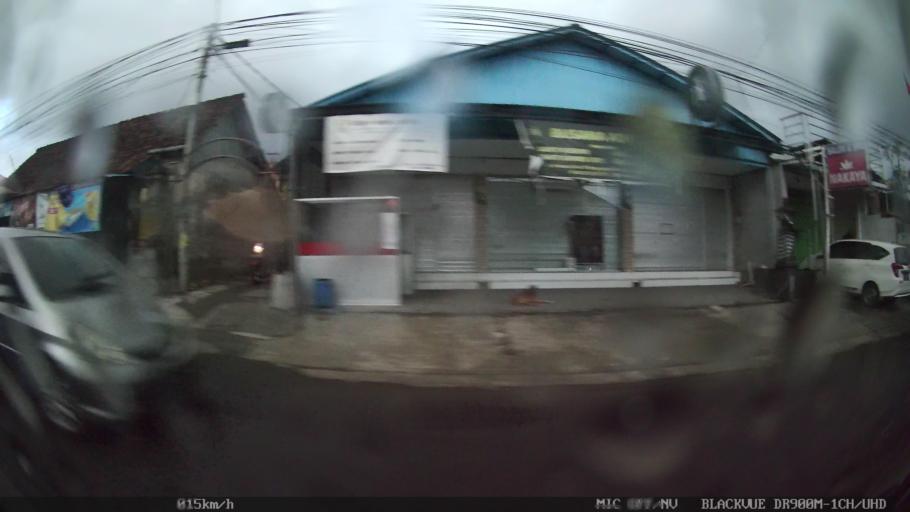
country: ID
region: Bali
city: Banjar Kayangan
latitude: -8.6198
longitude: 115.2229
